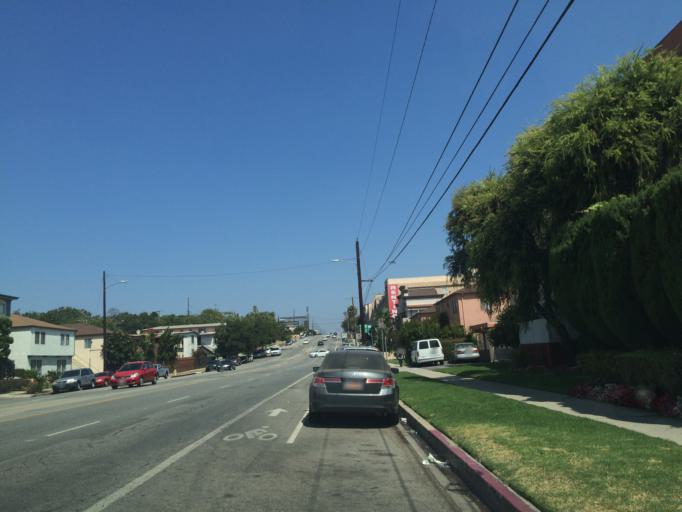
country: US
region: California
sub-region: Los Angeles County
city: Culver City
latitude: 34.0136
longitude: -118.4176
